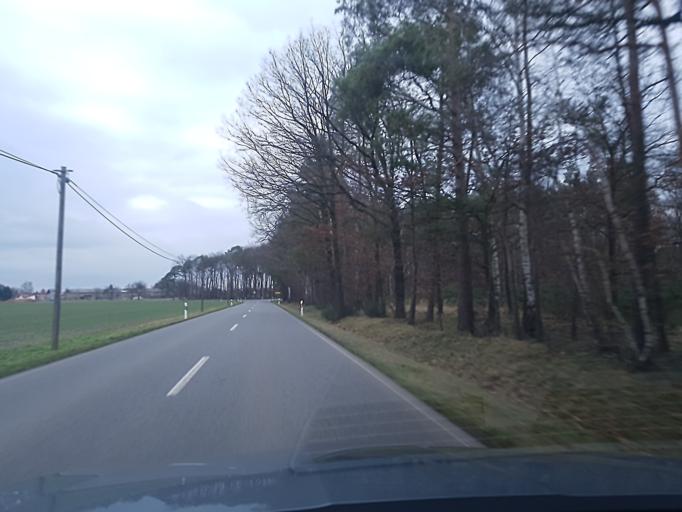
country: DE
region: Brandenburg
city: Sonnewalde
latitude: 51.6825
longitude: 13.6854
